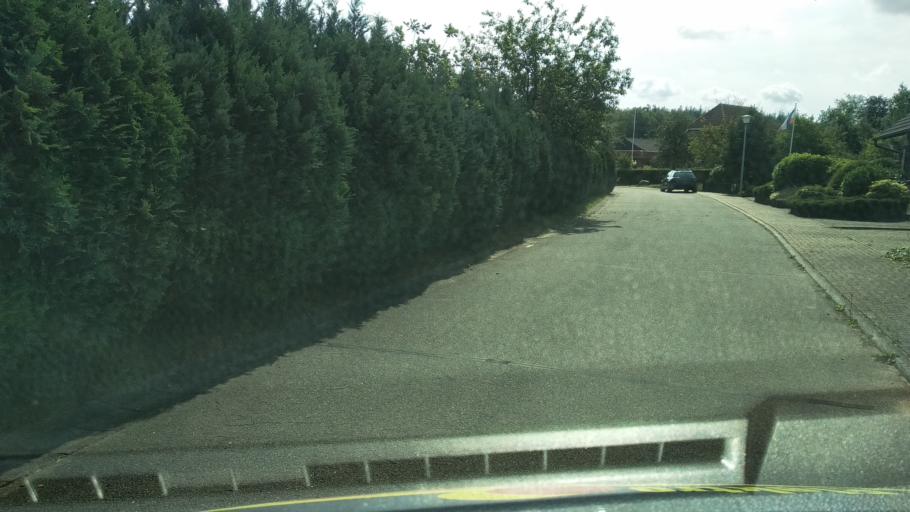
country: DE
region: Schleswig-Holstein
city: Brekendorf
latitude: 54.4200
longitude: 9.6364
